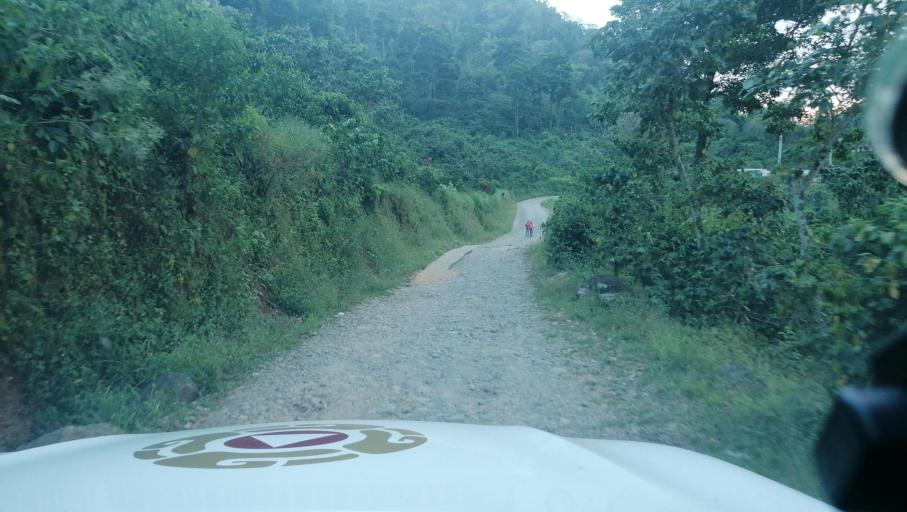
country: MX
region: Chiapas
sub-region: Cacahoatan
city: Benito Juarez
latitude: 15.0664
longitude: -92.2346
